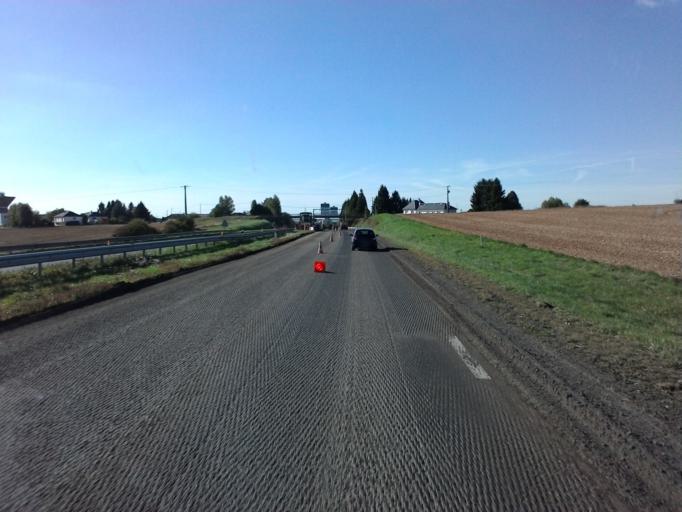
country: FR
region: Lorraine
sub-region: Departement de Meurthe-et-Moselle
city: Haucourt-Moulaine
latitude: 49.5009
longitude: 5.7983
